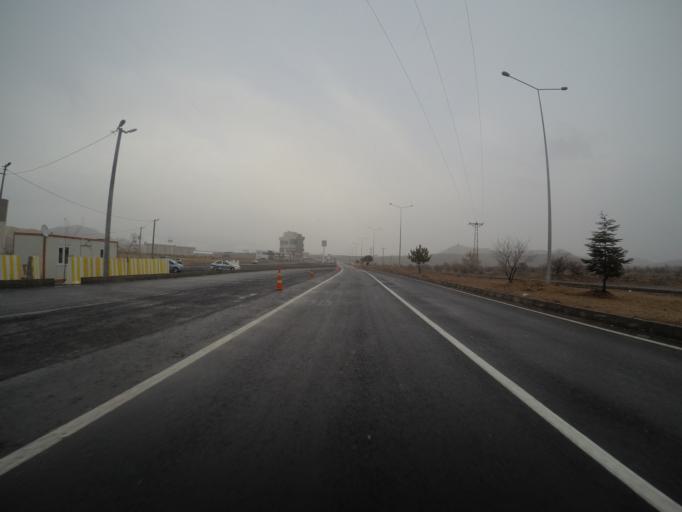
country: TR
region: Nevsehir
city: Nevsehir
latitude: 38.6730
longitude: 34.7514
